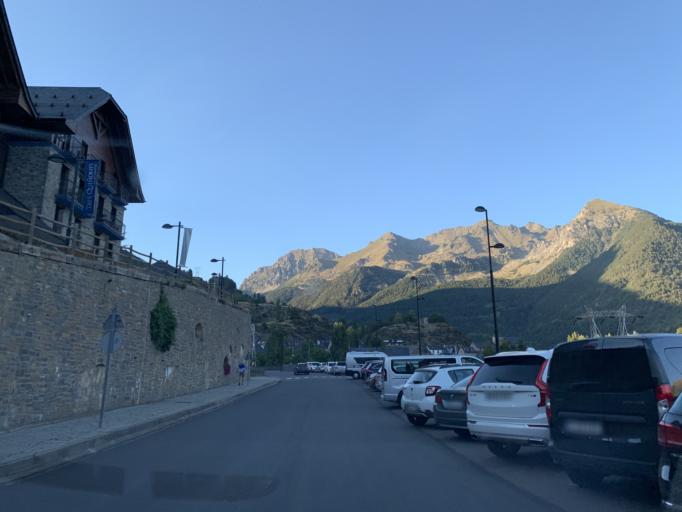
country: ES
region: Aragon
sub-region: Provincia de Huesca
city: Sallent de Gallego
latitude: 42.7693
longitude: -0.3346
